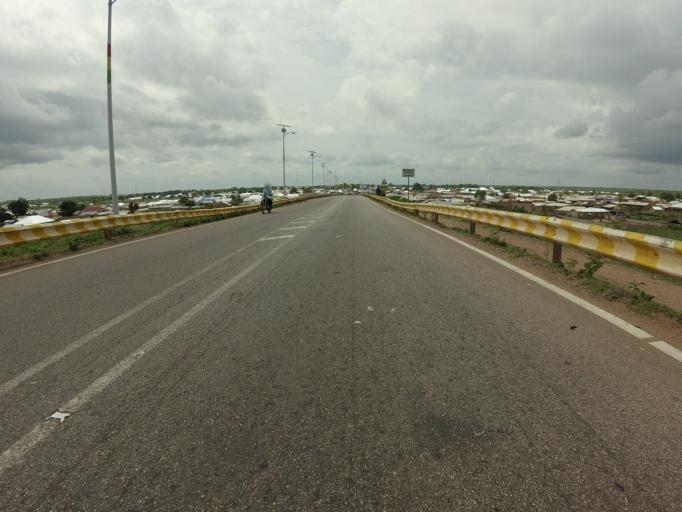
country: GH
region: Brong-Ahafo
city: Kintampo
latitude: 8.7674
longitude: -1.4545
